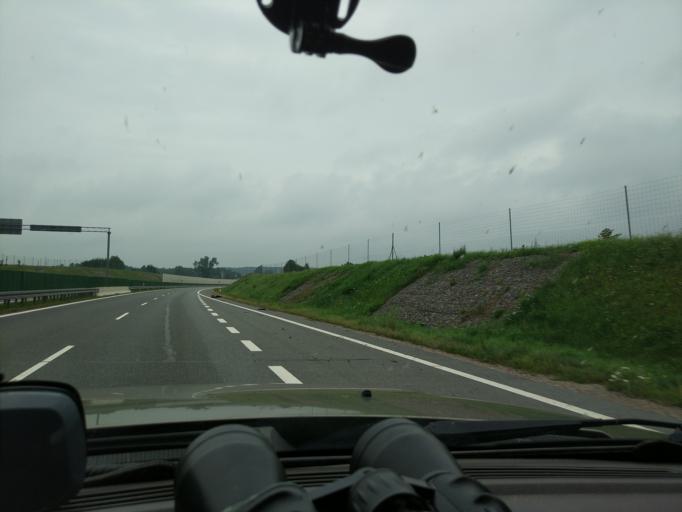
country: PL
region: Podlasie
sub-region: Powiat zambrowski
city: Zambrow
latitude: 52.9865
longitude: 22.2175
